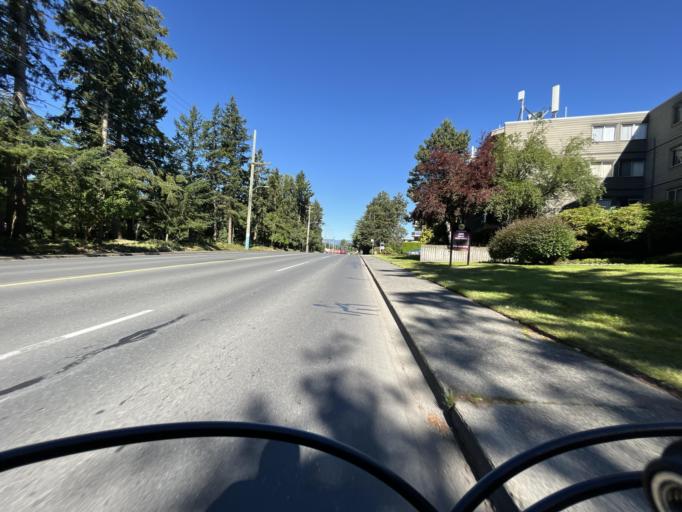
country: CA
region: British Columbia
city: Victoria
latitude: 48.4471
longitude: -123.3966
